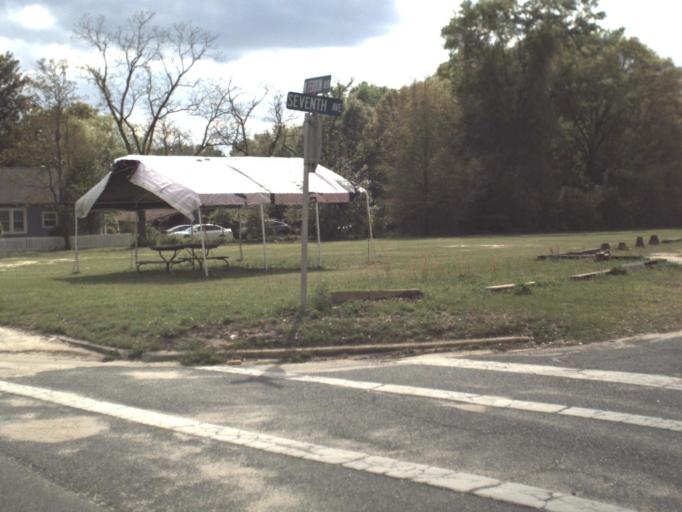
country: US
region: Florida
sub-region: Okaloosa County
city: Crestview
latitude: 30.7723
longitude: -86.5654
